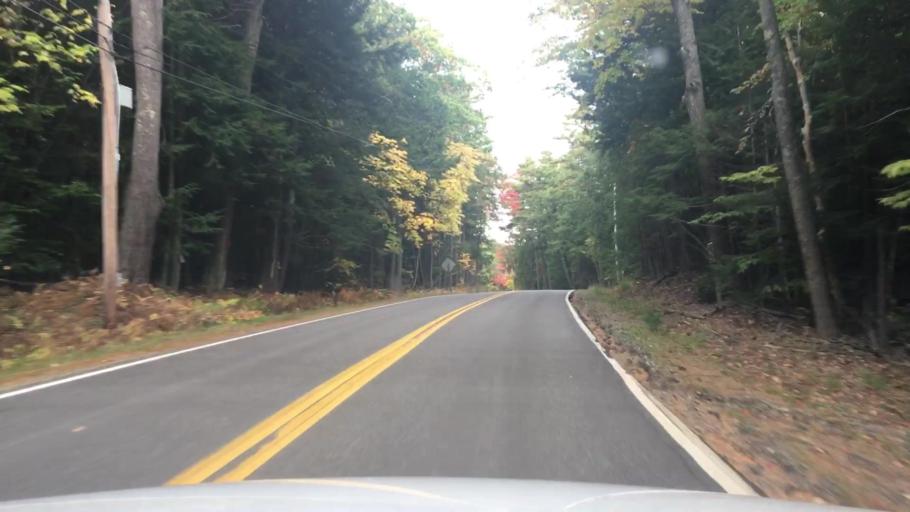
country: US
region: Maine
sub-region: Knox County
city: Camden
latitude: 44.2361
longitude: -69.1102
